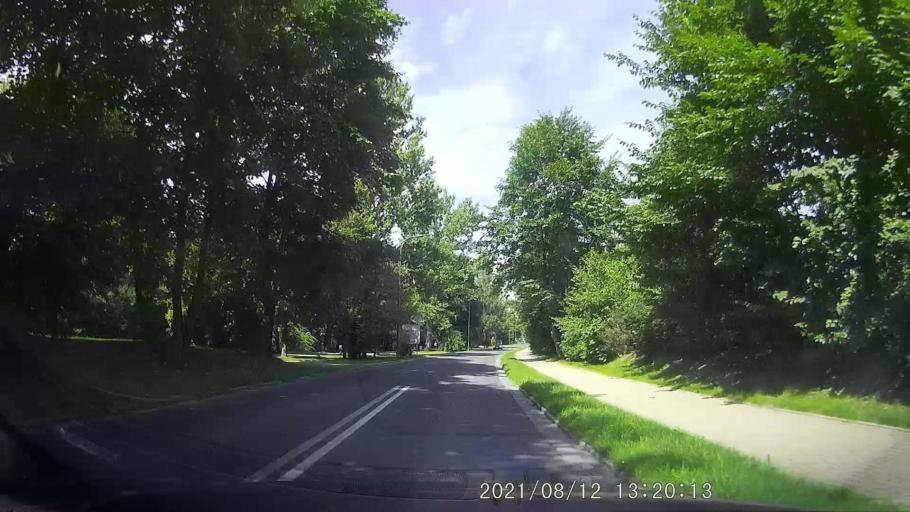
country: PL
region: Lower Silesian Voivodeship
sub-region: Powiat klodzki
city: Stronie Slaskie
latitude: 50.2856
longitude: 16.8780
